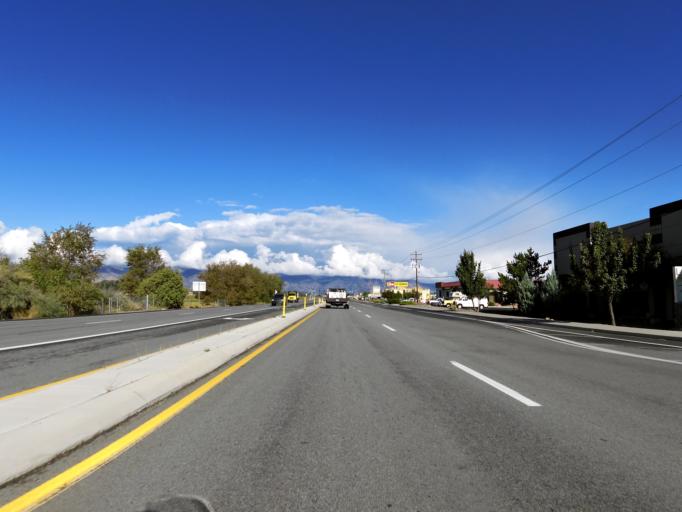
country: US
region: Nevada
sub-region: Douglas County
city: Gardnerville
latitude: 38.9206
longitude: -119.7223
